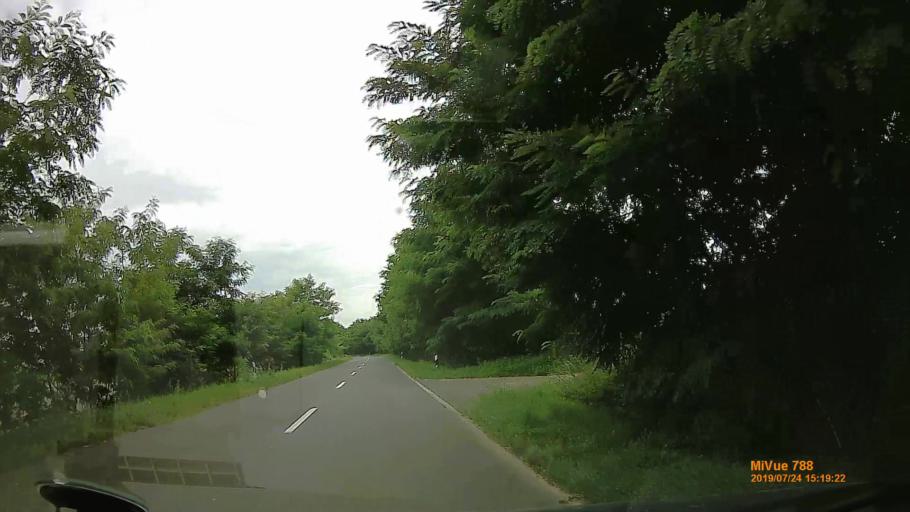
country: HU
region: Szabolcs-Szatmar-Bereg
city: Tarpa
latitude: 48.1706
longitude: 22.5436
